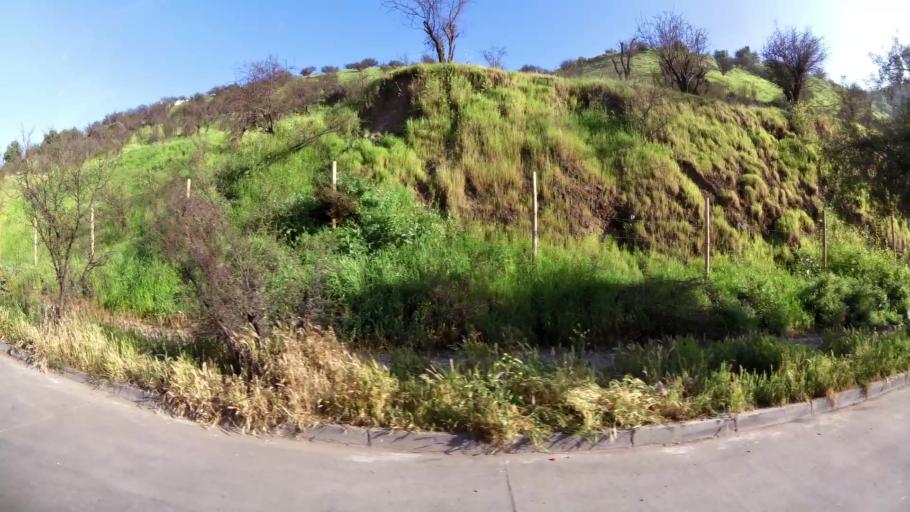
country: CL
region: Santiago Metropolitan
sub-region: Provincia de Chacabuco
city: Chicureo Abajo
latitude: -33.3692
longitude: -70.6511
